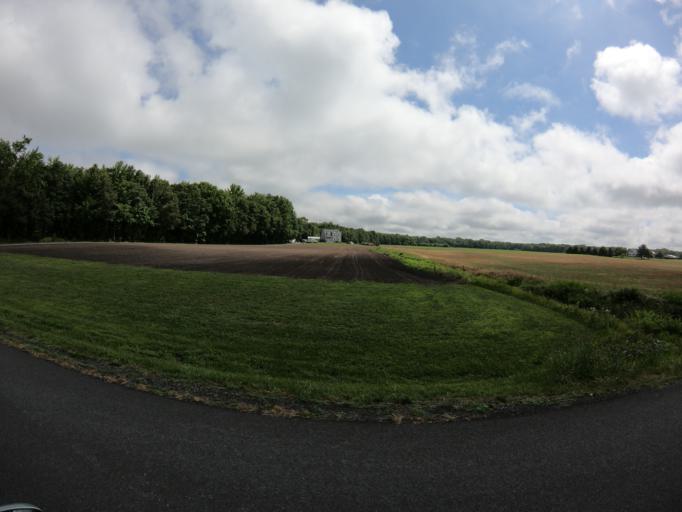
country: US
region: Maryland
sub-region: Caroline County
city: Greensboro
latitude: 39.0502
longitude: -75.8332
